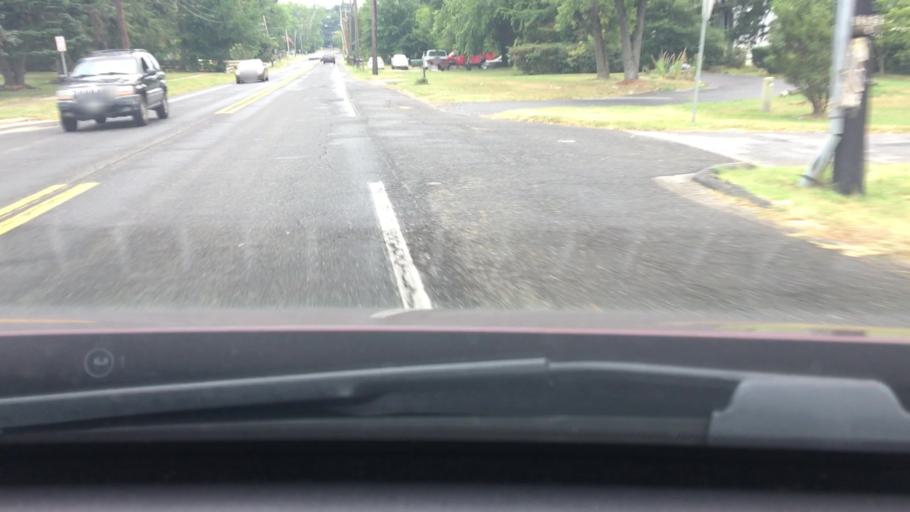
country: US
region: Maryland
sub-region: Prince George's County
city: Beltsville
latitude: 39.0474
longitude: -76.9167
